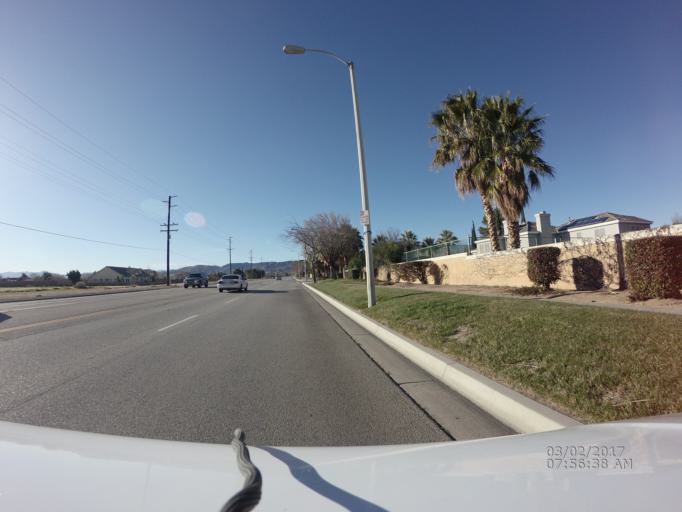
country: US
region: California
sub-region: Los Angeles County
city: Desert View Highlands
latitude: 34.6114
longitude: -118.1836
